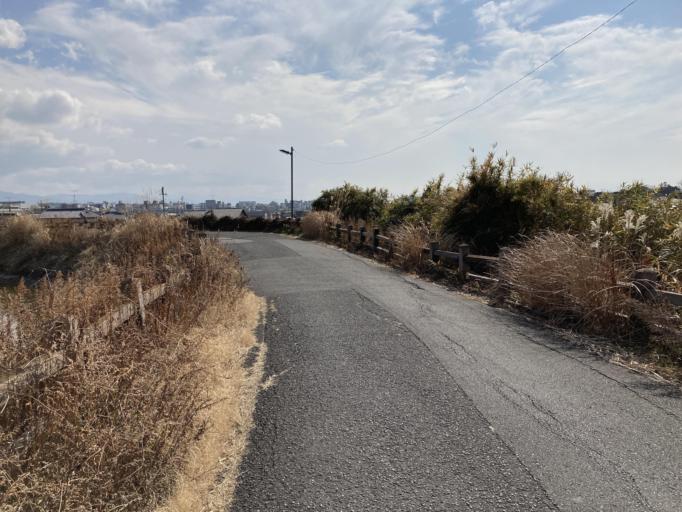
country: JP
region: Nara
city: Nara-shi
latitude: 34.6963
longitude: 135.8075
